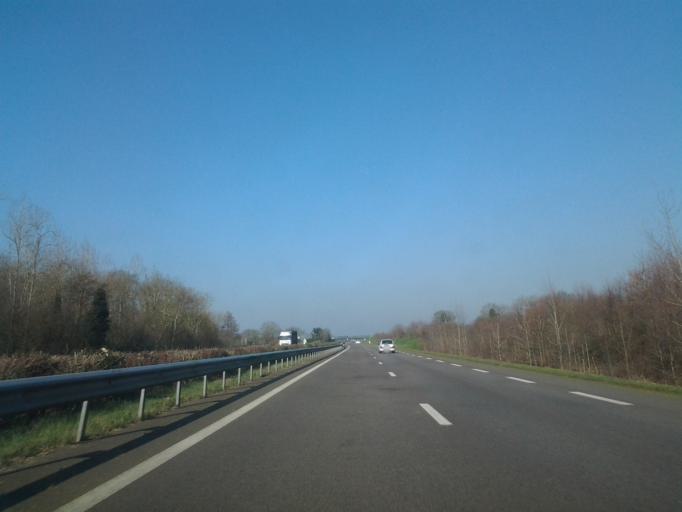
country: FR
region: Pays de la Loire
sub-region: Departement de la Vendee
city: Saint-Christophe-du-Ligneron
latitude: 46.8058
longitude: -1.7359
